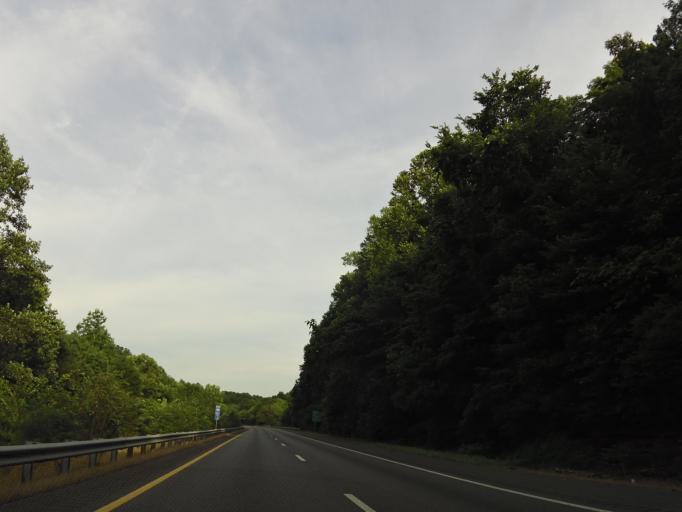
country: US
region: Tennessee
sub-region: Cheatham County
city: Pegram
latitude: 36.0801
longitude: -87.0407
